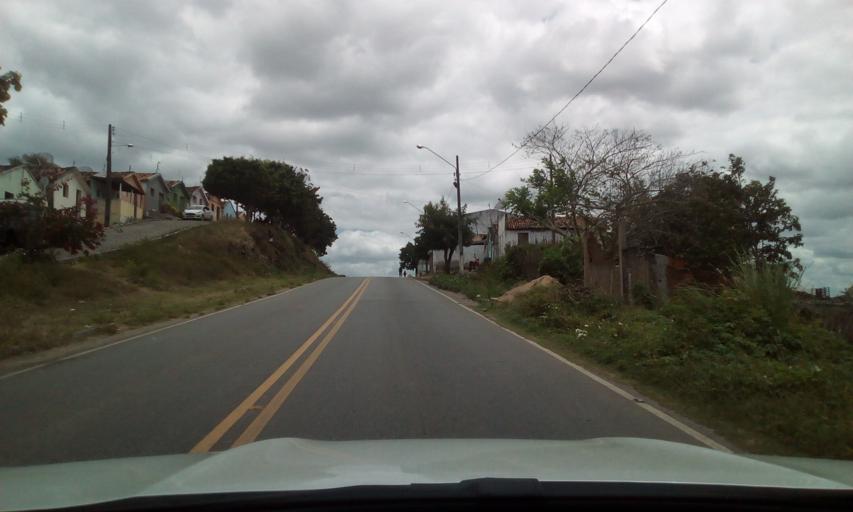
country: BR
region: Paraiba
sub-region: Serra Redonda
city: Alagoa Grande
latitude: -7.1676
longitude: -35.5916
